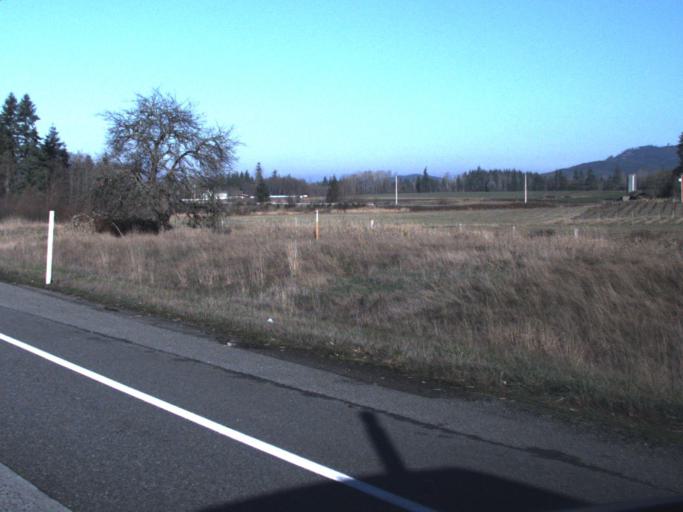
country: US
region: Washington
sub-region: Snohomish County
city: Stanwood
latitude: 48.3057
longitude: -122.3130
